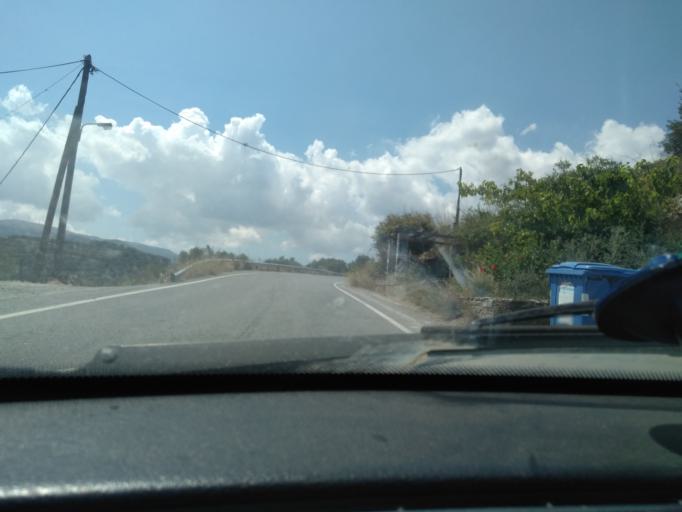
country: GR
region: Crete
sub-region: Nomos Lasithiou
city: Siteia
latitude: 35.1420
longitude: 26.0804
